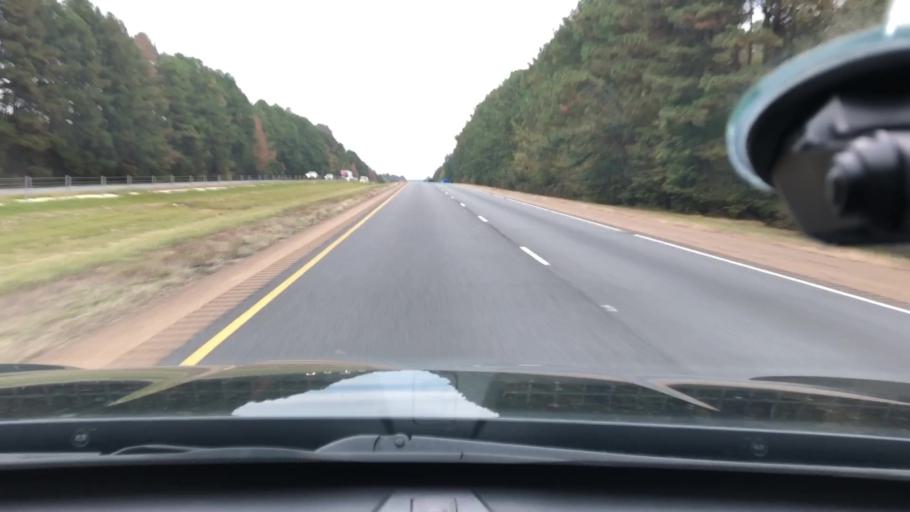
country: US
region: Arkansas
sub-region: Clark County
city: Gurdon
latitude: 33.9746
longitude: -93.2058
